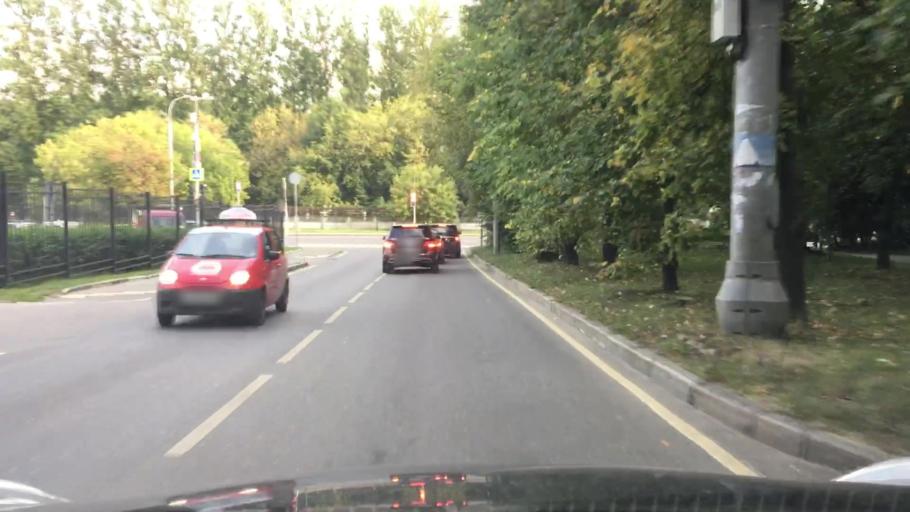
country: RU
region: Moscow
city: Davydkovo
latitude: 55.7344
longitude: 37.4556
